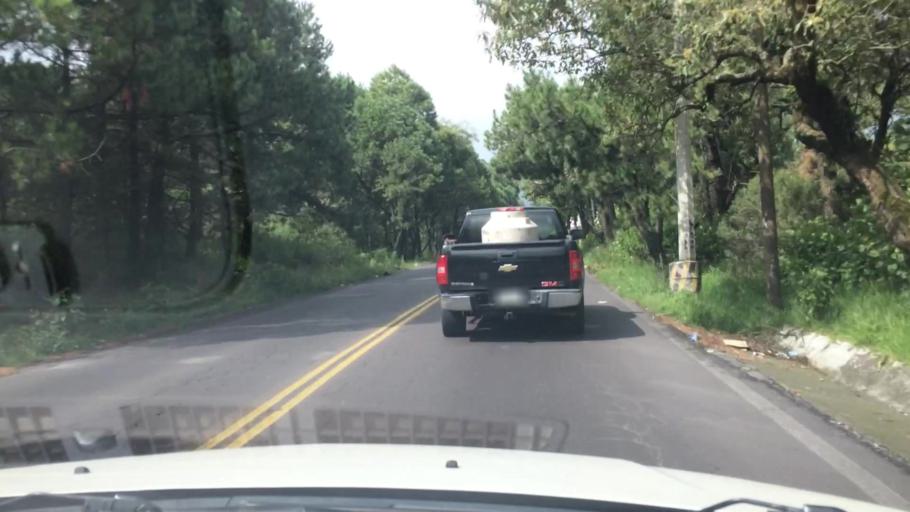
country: MX
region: Mexico City
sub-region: Tlalpan
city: Lomas de Tepemecatl
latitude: 19.2590
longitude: -99.2380
